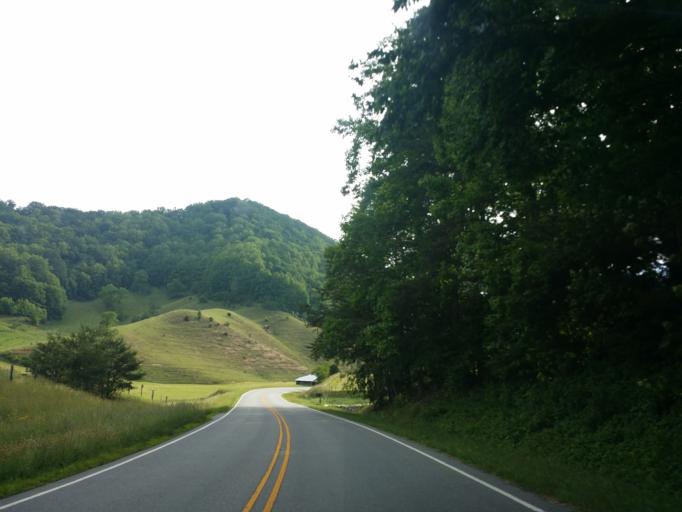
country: US
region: North Carolina
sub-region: Madison County
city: Marshall
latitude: 35.6997
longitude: -82.8137
